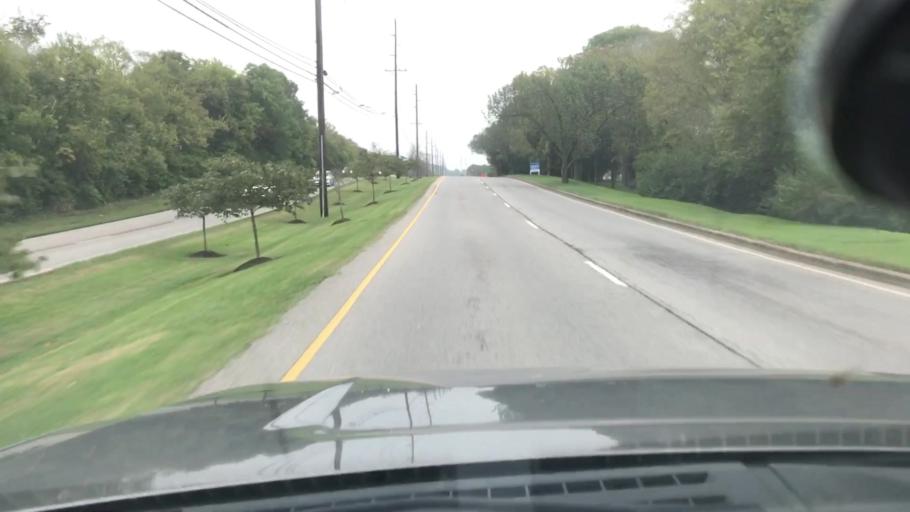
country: US
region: Tennessee
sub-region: Williamson County
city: Brentwood
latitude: 36.0385
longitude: -86.8048
